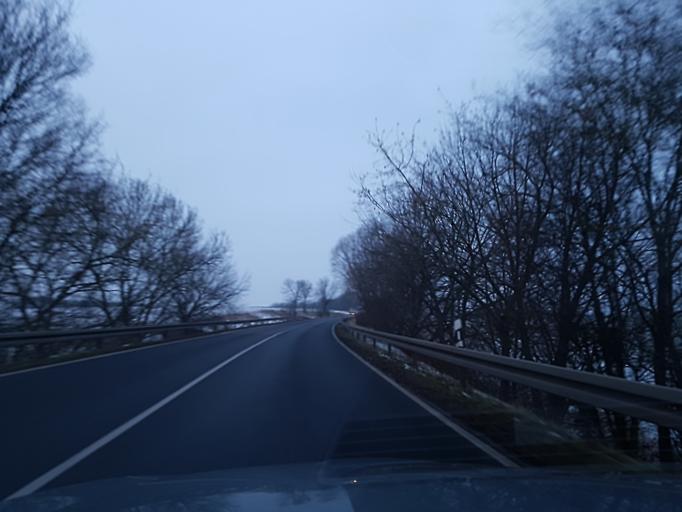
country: DE
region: Saxony
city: Ostrau
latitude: 51.1923
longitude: 13.1491
